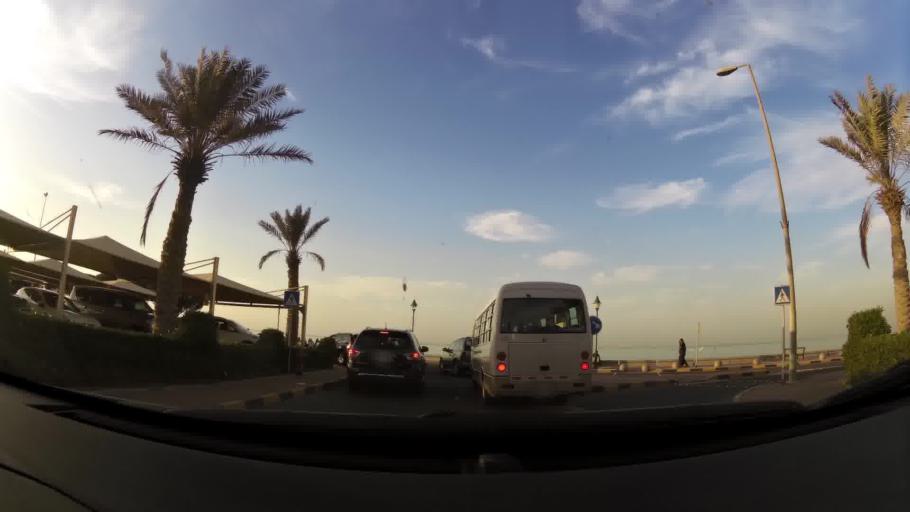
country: KW
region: Al Asimah
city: Kuwait City
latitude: 29.3911
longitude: 47.9823
